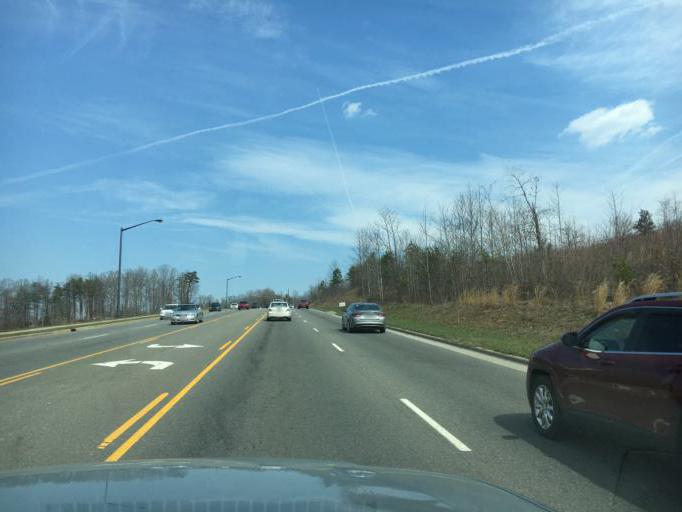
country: US
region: North Carolina
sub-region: McDowell County
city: West Marion
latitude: 35.6655
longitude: -82.0211
